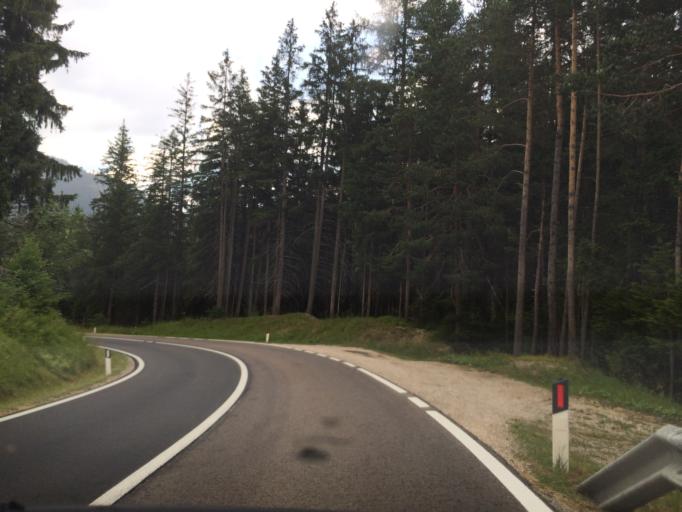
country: IT
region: Trentino-Alto Adige
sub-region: Bolzano
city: Badia
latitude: 46.6177
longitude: 11.8937
